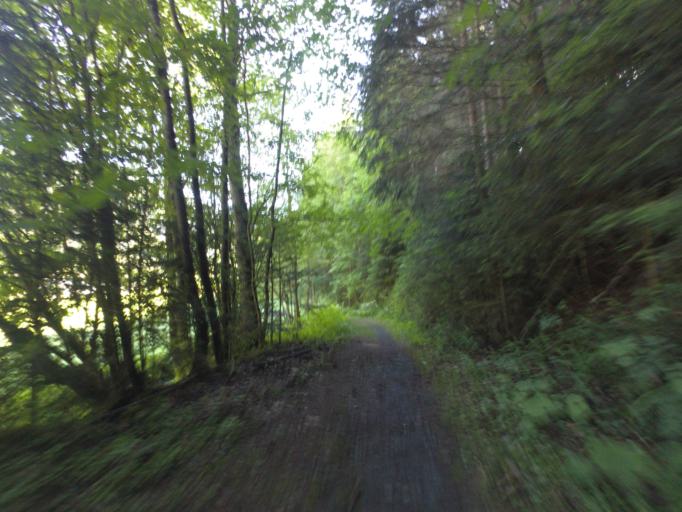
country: AT
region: Salzburg
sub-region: Politischer Bezirk Sankt Johann im Pongau
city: Goldegg
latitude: 47.3252
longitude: 13.0813
